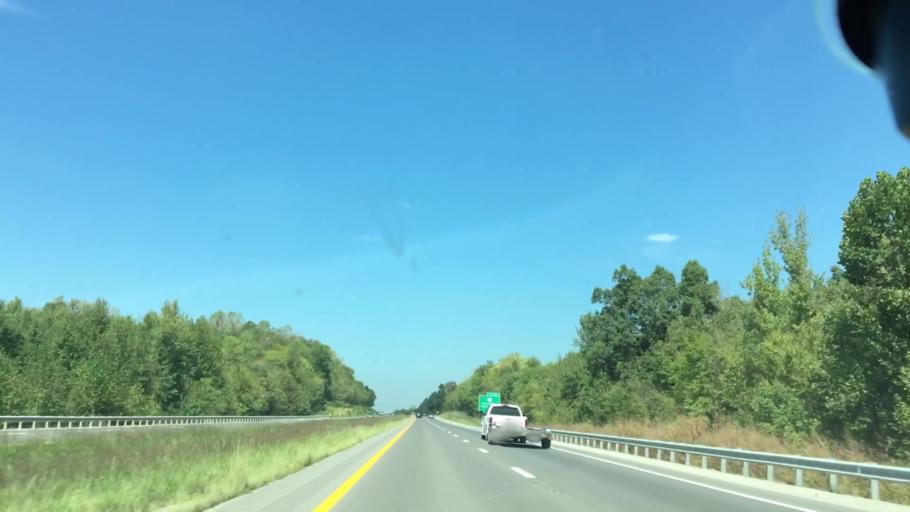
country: US
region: Kentucky
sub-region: Hopkins County
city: Earlington
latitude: 37.2762
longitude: -87.4555
